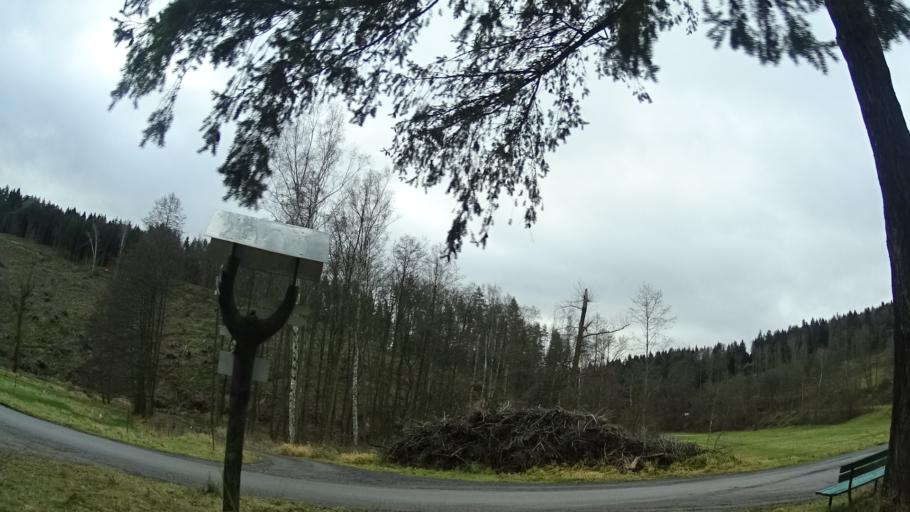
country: DE
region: Thuringia
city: Herschdorf
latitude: 50.7134
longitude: 11.4936
